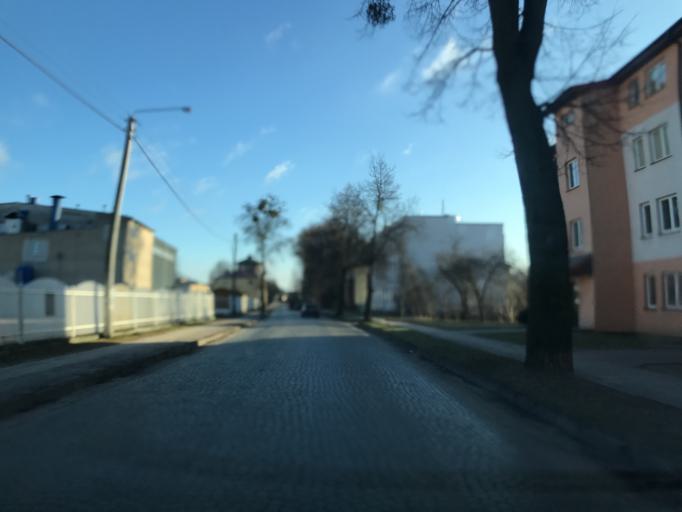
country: PL
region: Warmian-Masurian Voivodeship
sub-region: Powiat ostrodzki
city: Ostroda
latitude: 53.6979
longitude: 19.9468
